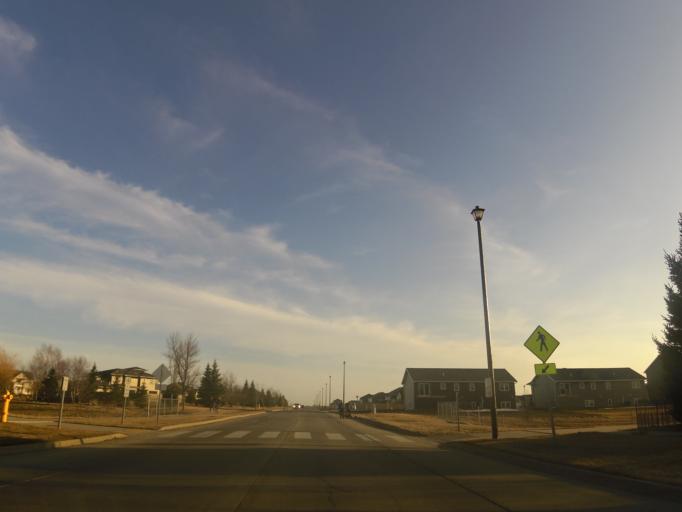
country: US
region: North Dakota
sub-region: Grand Forks County
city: Grand Forks
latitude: 47.8711
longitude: -97.0378
